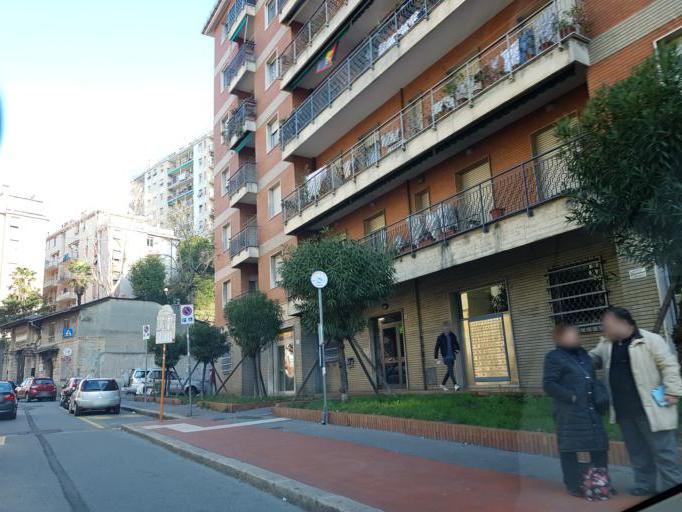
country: IT
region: Liguria
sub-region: Provincia di Genova
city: Manesseno
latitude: 44.4609
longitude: 8.9021
